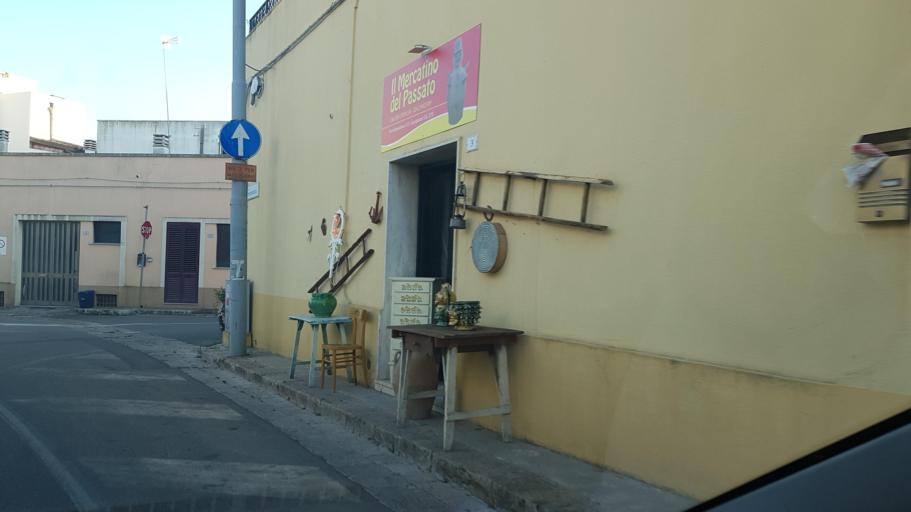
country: IT
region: Apulia
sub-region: Provincia di Lecce
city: Lucugnano
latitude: 39.9350
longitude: 18.3192
